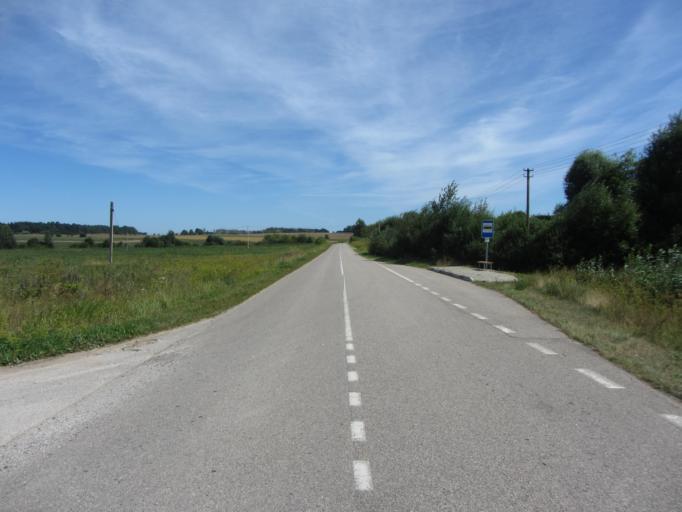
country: LT
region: Utenos apskritis
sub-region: Utena
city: Utena
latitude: 55.6531
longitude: 25.5216
